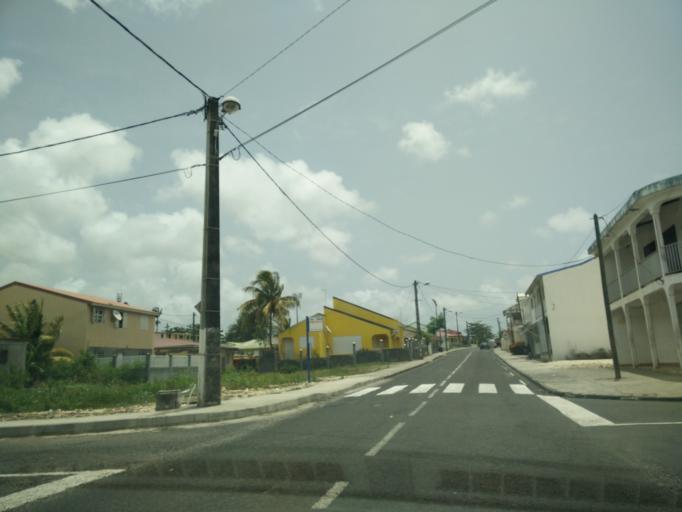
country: GP
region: Guadeloupe
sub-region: Guadeloupe
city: Petit-Canal
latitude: 16.3808
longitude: -61.4869
